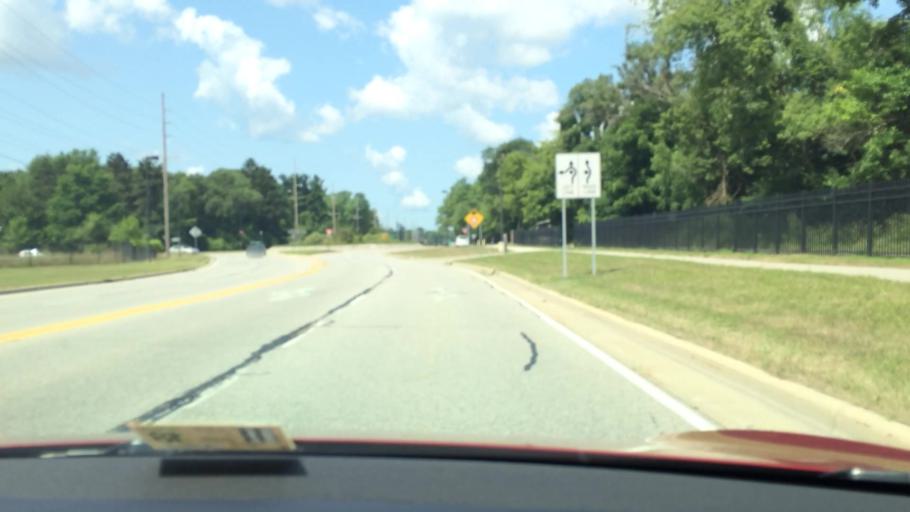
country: US
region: Indiana
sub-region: Saint Joseph County
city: Notre Dame
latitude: 41.7090
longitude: -86.2261
